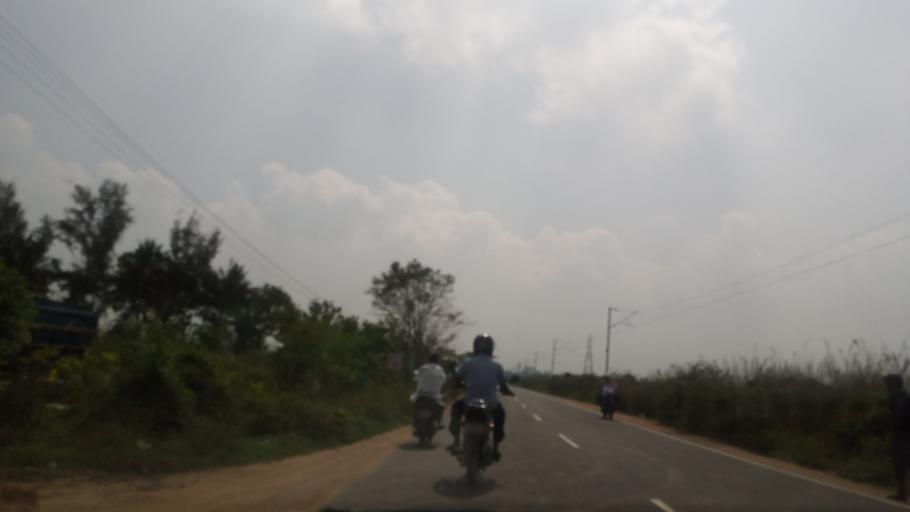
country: IN
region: Tamil Nadu
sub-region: Kancheepuram
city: Kanchipuram
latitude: 12.8913
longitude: 79.6865
